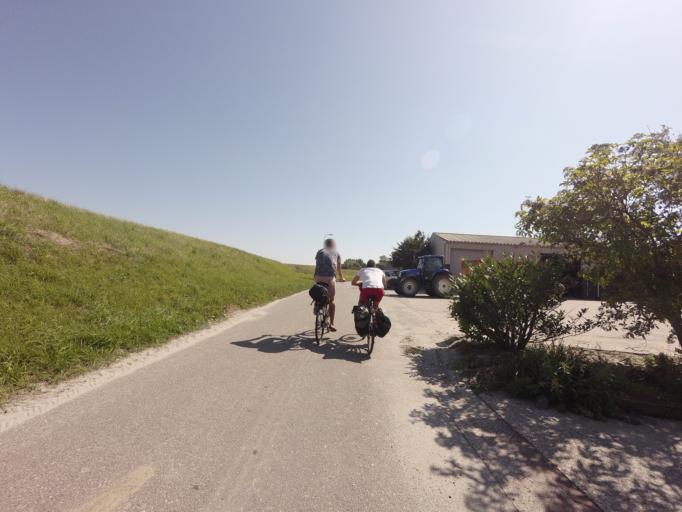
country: NL
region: Friesland
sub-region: Gemeente Dongeradeel
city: Anjum
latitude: 53.3956
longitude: 6.1084
